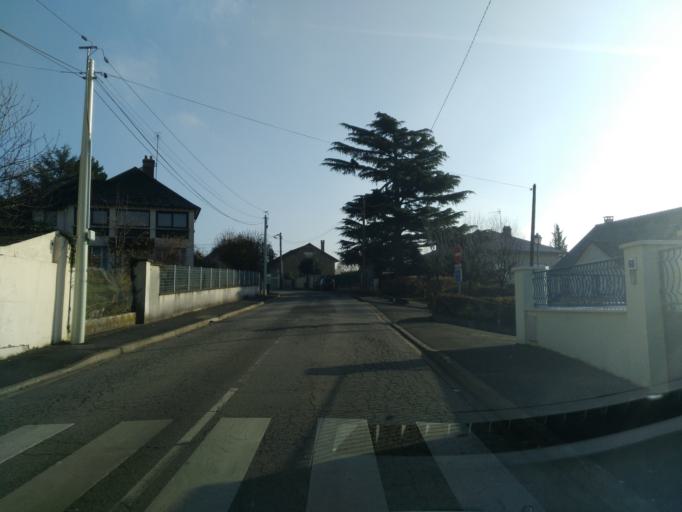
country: FR
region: Ile-de-France
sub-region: Departement des Yvelines
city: Feucherolles
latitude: 48.8745
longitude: 1.9752
